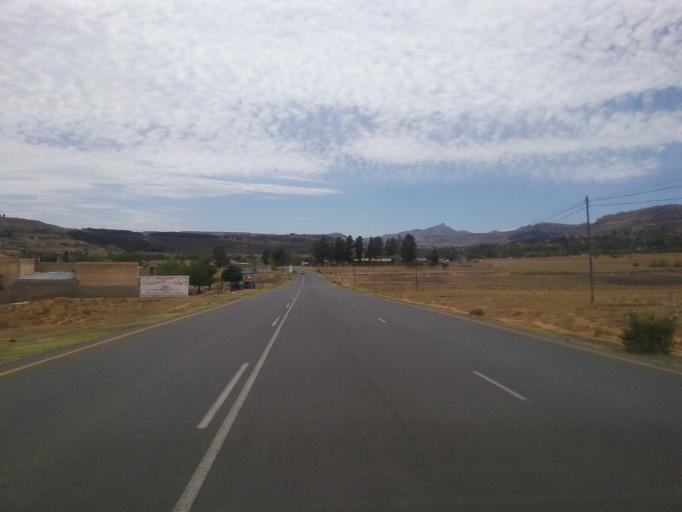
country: LS
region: Maseru
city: Nako
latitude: -29.6251
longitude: 27.4913
